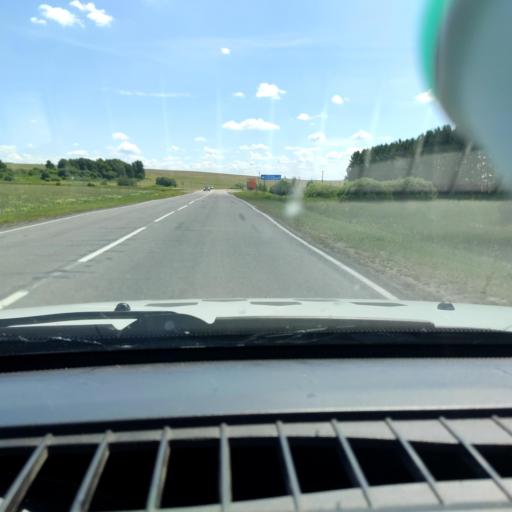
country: RU
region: Bashkortostan
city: Verkhniye Kigi
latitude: 55.3689
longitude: 58.6839
